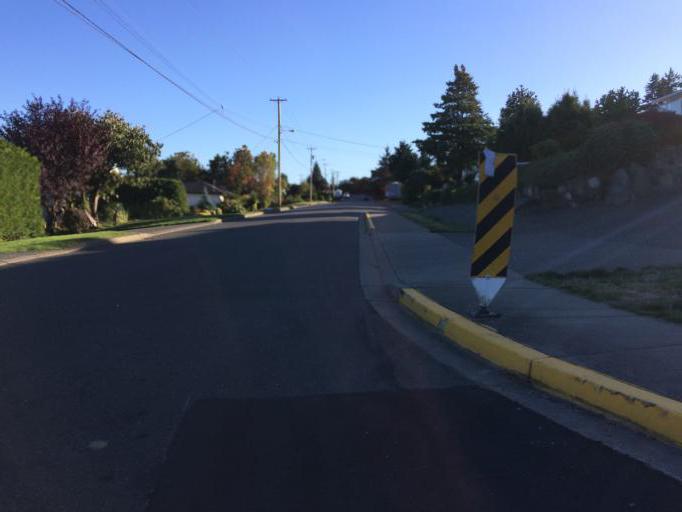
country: CA
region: British Columbia
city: Campbell River
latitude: 50.0028
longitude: -125.2357
